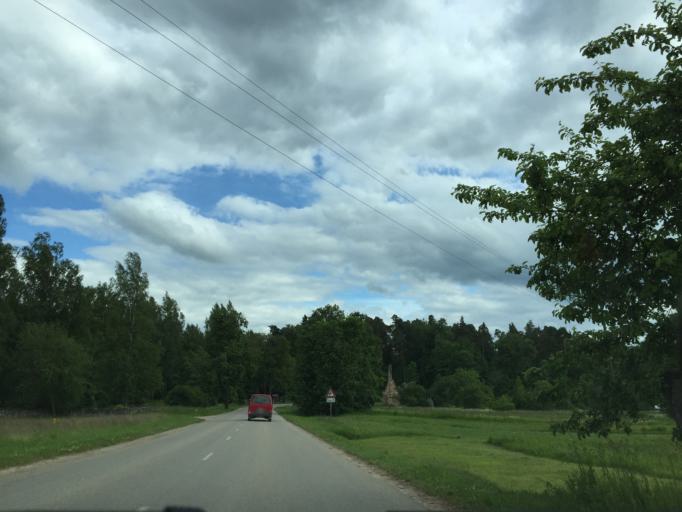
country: LV
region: Apes Novads
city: Ape
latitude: 57.5135
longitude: 26.4041
